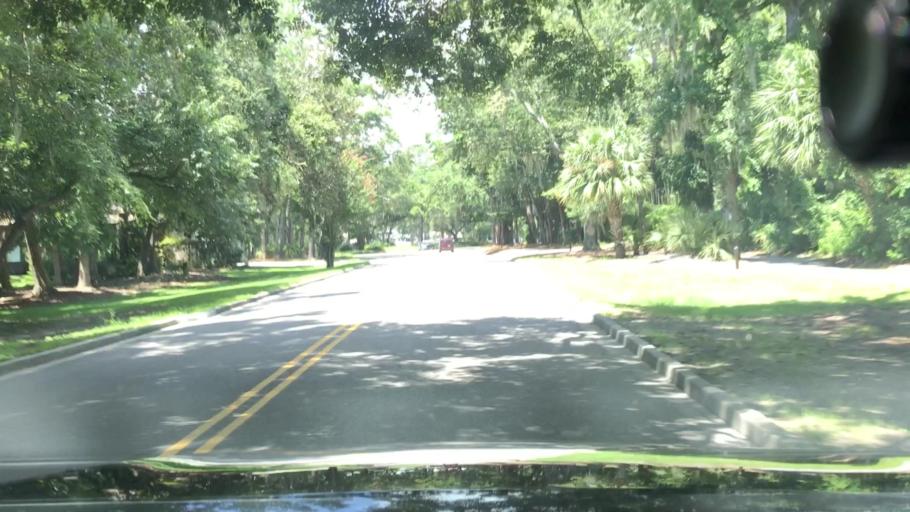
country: US
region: South Carolina
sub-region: Beaufort County
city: Hilton Head Island
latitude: 32.1319
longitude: -80.7985
